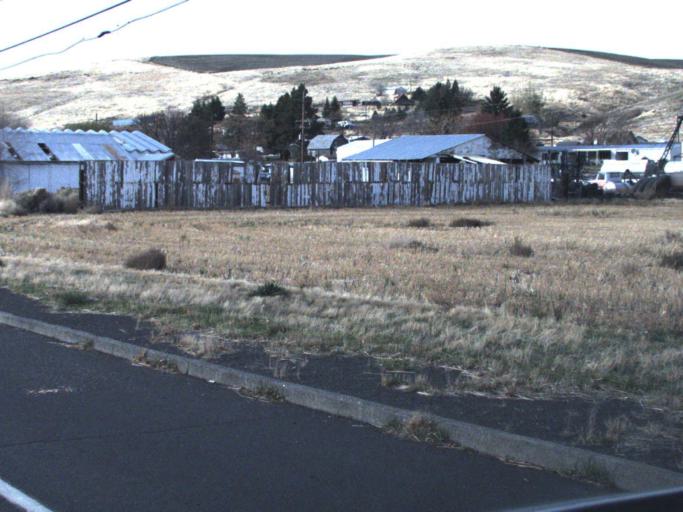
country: US
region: Washington
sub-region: Garfield County
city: Pomeroy
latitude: 46.4748
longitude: -117.5739
